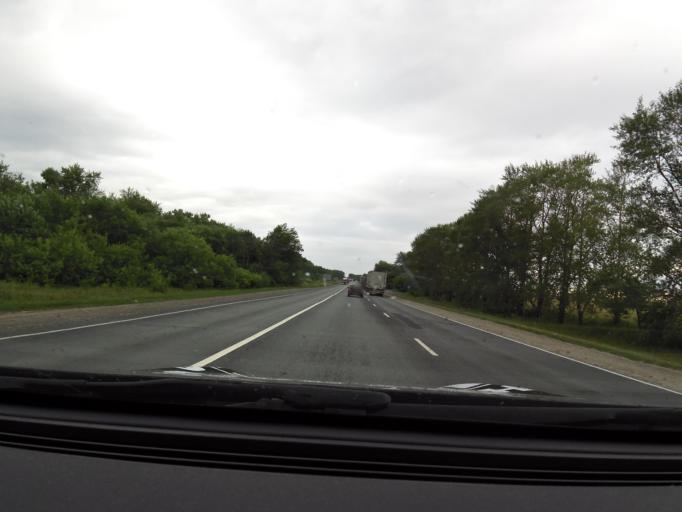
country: RU
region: Chuvashia
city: Yantikovo
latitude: 55.7898
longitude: 47.7545
